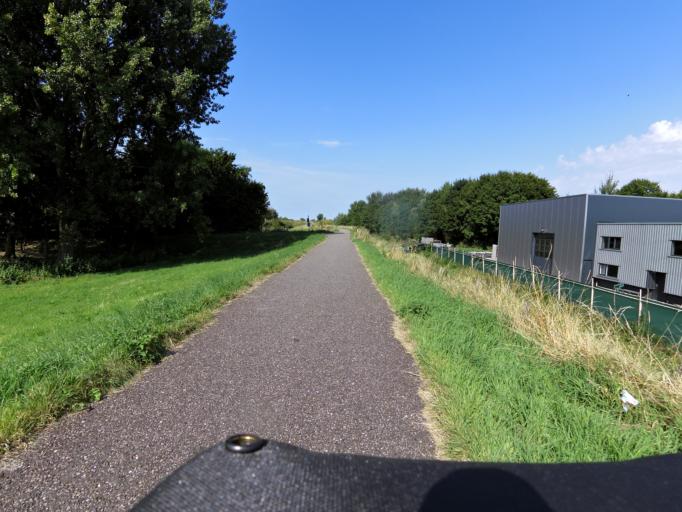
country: NL
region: South Holland
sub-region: Gemeente Oud-Beijerland
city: Oud-Beijerland
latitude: 51.8264
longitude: 4.4268
